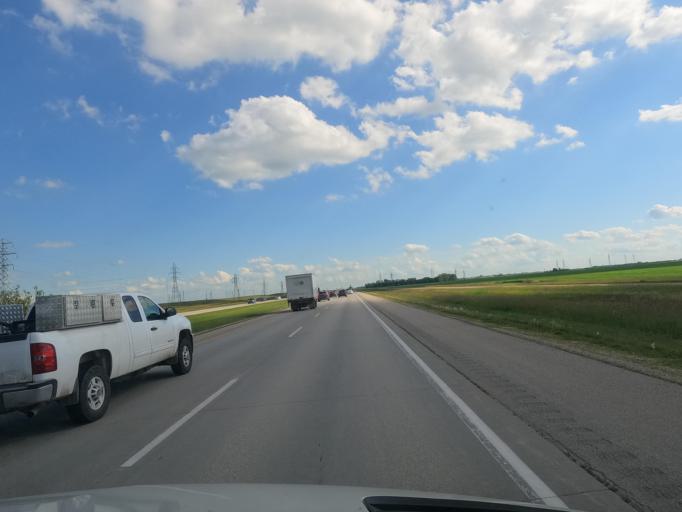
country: CA
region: Manitoba
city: Winnipeg
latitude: 49.8795
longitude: -96.9589
